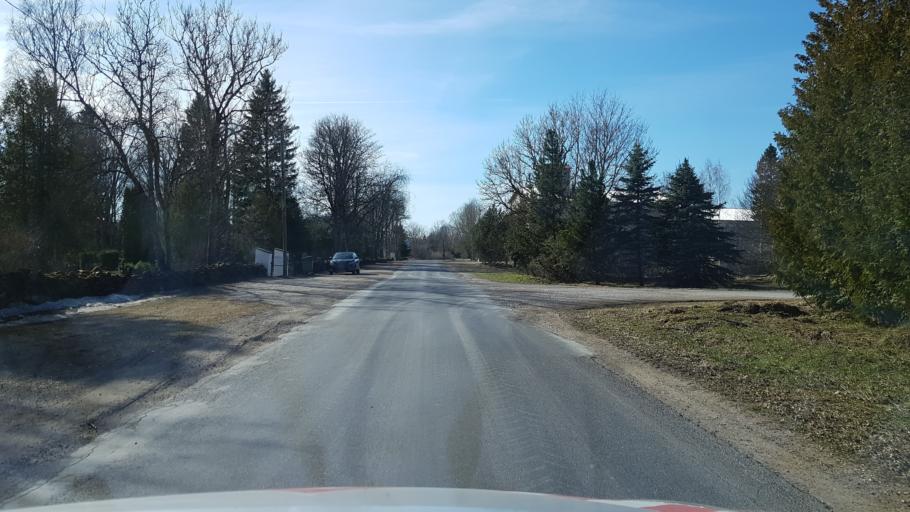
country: EE
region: Harju
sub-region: Nissi vald
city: Riisipere
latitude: 59.1001
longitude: 24.3206
